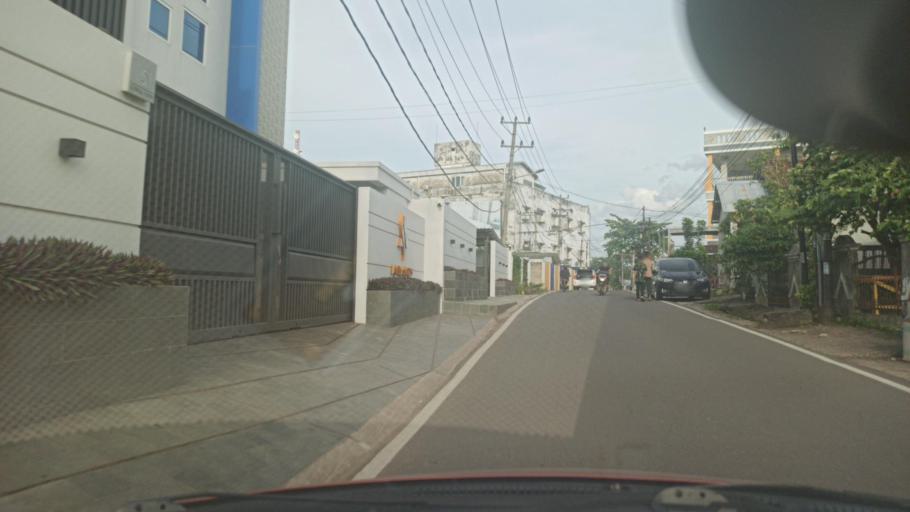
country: ID
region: South Sumatra
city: Palembang
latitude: -2.9803
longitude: 104.7229
